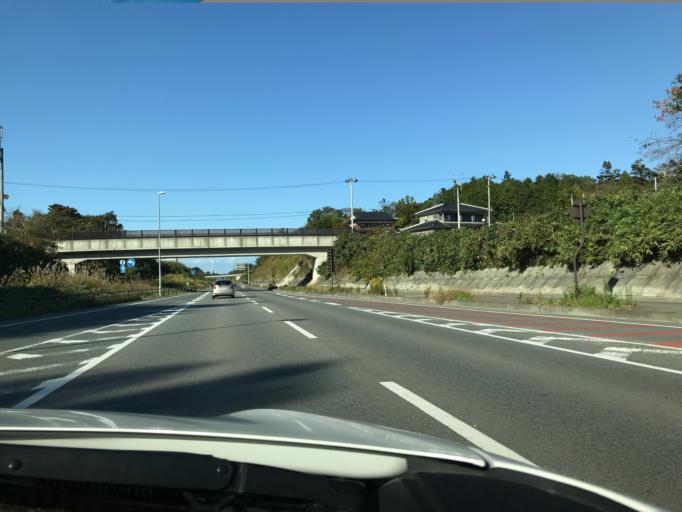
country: JP
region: Miyagi
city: Marumori
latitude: 37.8091
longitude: 140.9434
